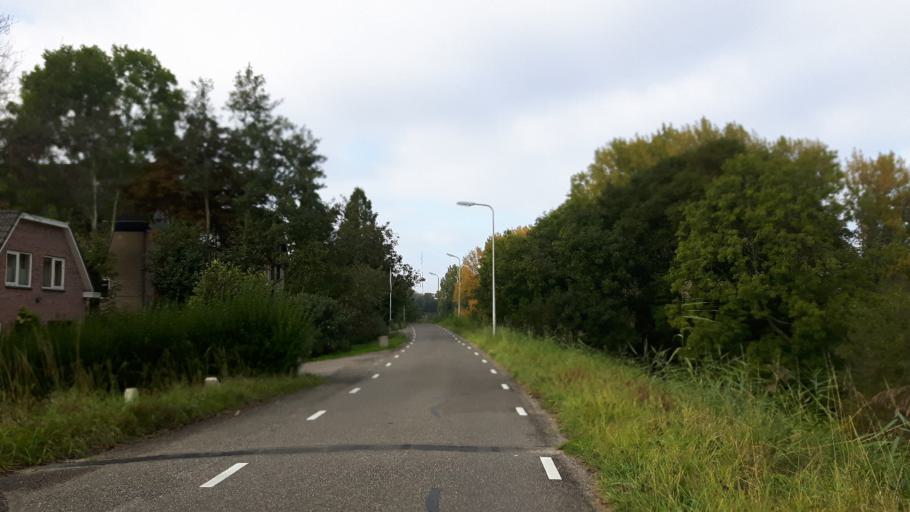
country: NL
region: South Holland
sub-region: Gemeente Gouda
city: Gouda
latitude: 52.0074
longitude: 4.7375
